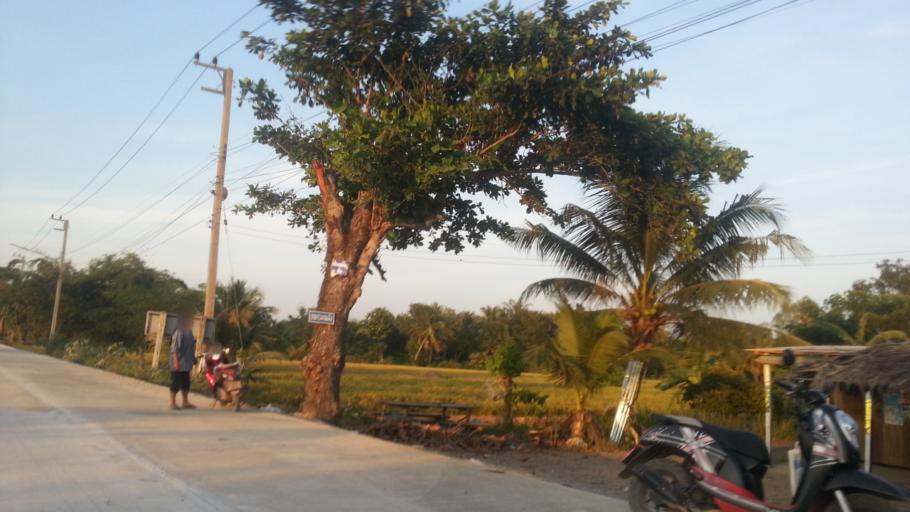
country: TH
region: Pathum Thani
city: Nong Suea
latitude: 14.0396
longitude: 100.8665
